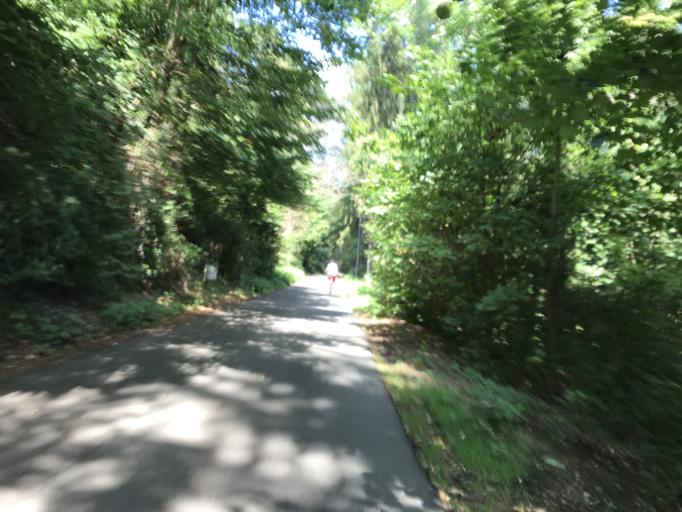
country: DE
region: Rheinland-Pfalz
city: Bad Munster am Stein-Ebernburg
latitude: 49.8301
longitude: 7.8475
